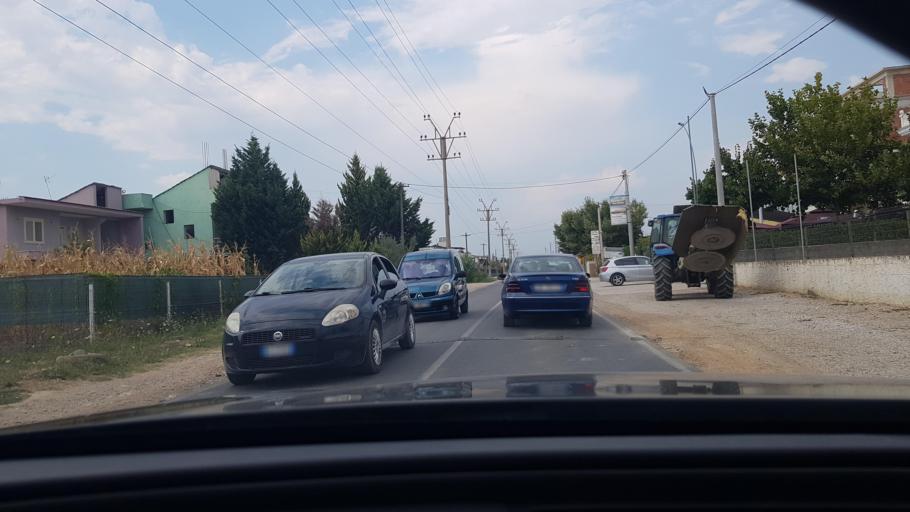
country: AL
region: Durres
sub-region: Rrethi i Durresit
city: Sukth
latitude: 41.3996
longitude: 19.5466
